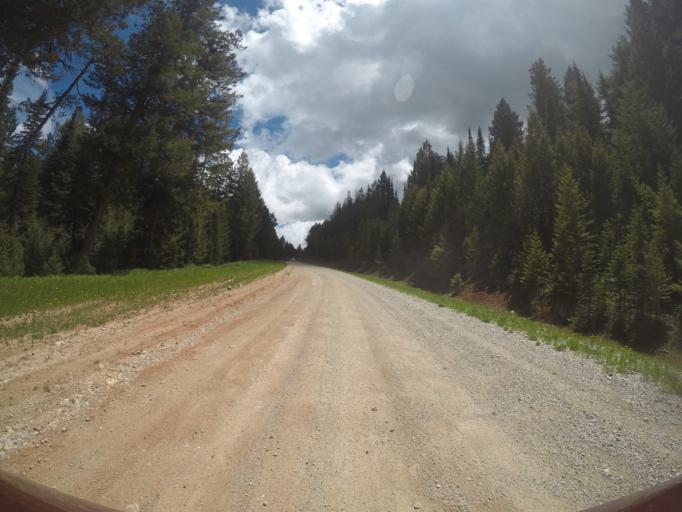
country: US
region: Wyoming
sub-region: Big Horn County
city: Lovell
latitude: 45.1824
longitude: -108.4700
